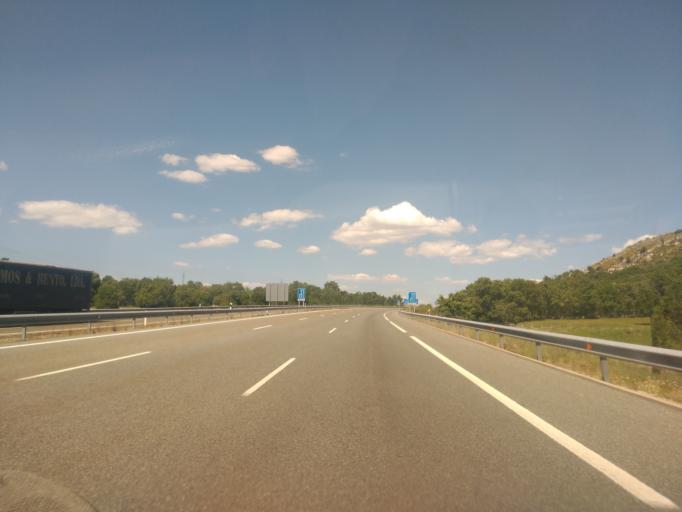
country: ES
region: Castille and Leon
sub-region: Provincia de Salamanca
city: Vallejera de Riofrio
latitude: 40.4174
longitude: -5.7134
